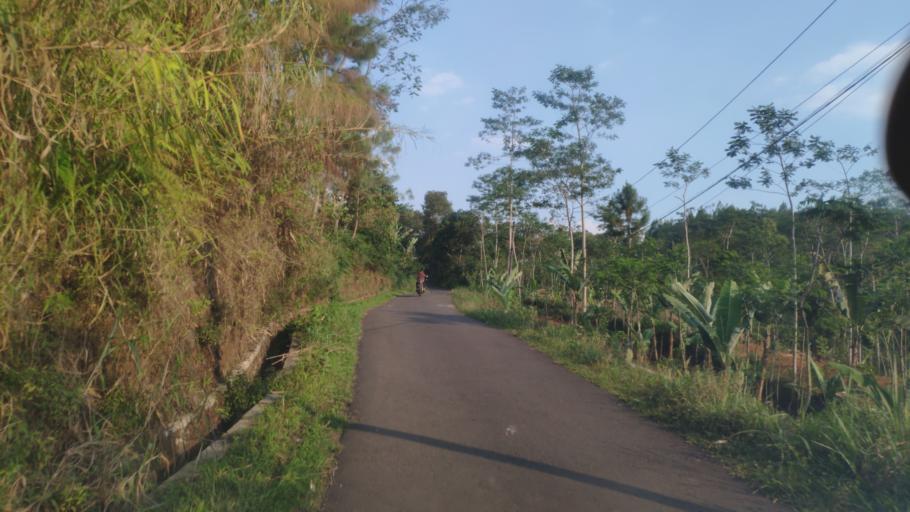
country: ID
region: Central Java
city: Wonosobo
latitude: -7.2551
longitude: 109.6895
